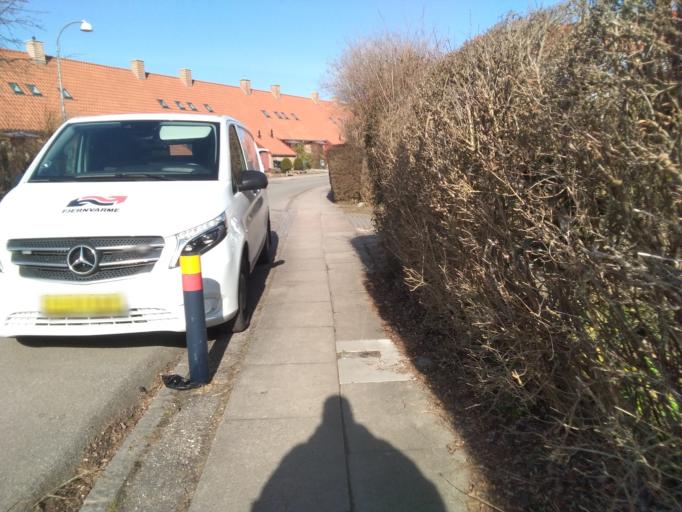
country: DK
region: Capital Region
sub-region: Gladsaxe Municipality
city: Buddinge
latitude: 55.7514
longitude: 12.4628
